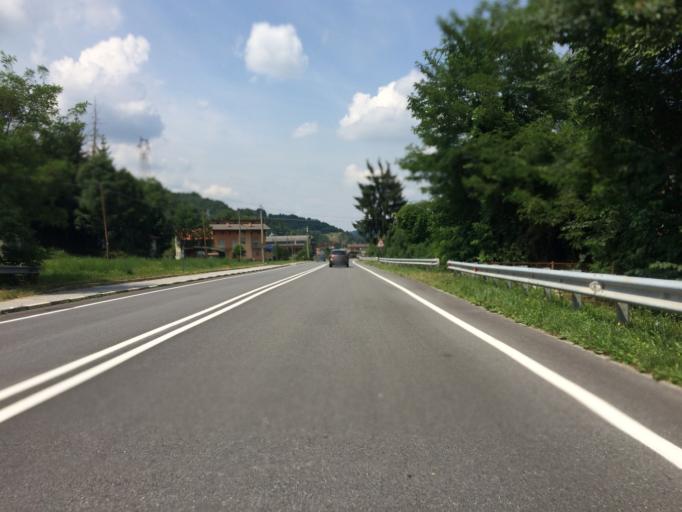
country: IT
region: Piedmont
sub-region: Provincia di Cuneo
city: Robilante
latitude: 44.2756
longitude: 7.5186
